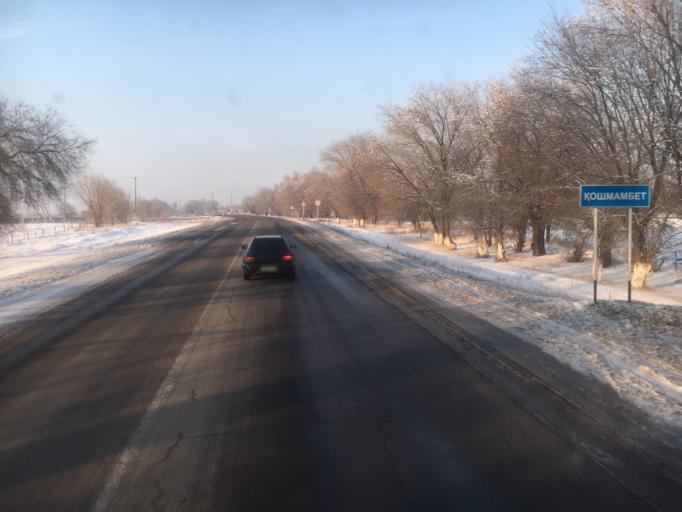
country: KZ
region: Almaty Oblysy
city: Burunday
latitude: 43.3297
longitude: 76.6622
